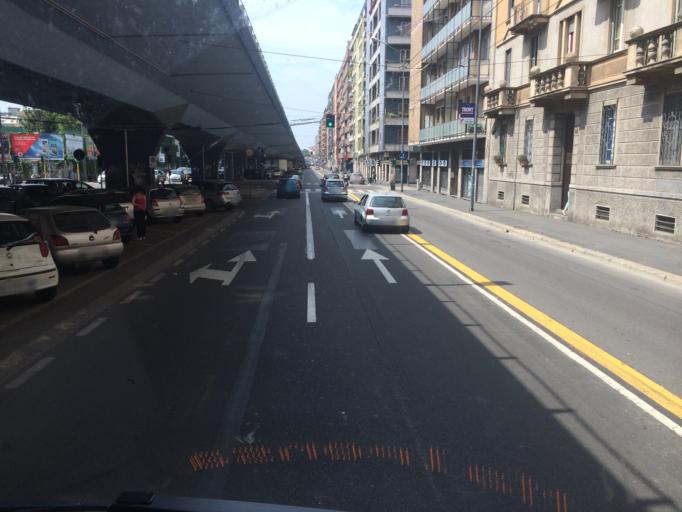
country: IT
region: Lombardy
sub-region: Citta metropolitana di Milano
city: Novate Milanese
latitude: 45.4930
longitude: 9.1559
